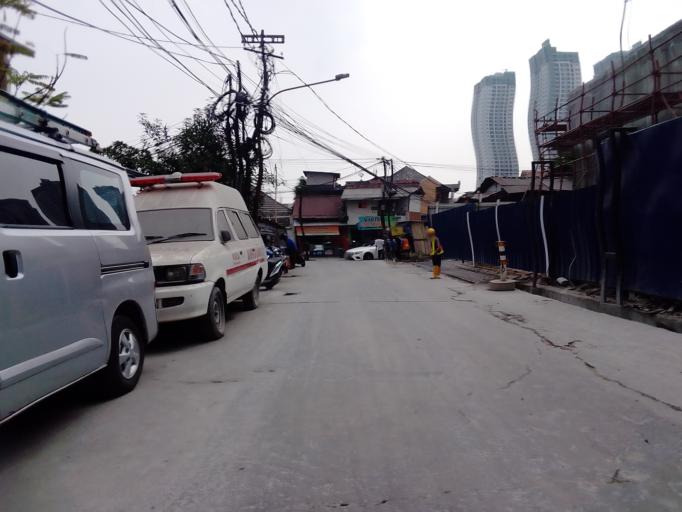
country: ID
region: Jakarta Raya
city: Jakarta
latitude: -6.1995
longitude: 106.8207
